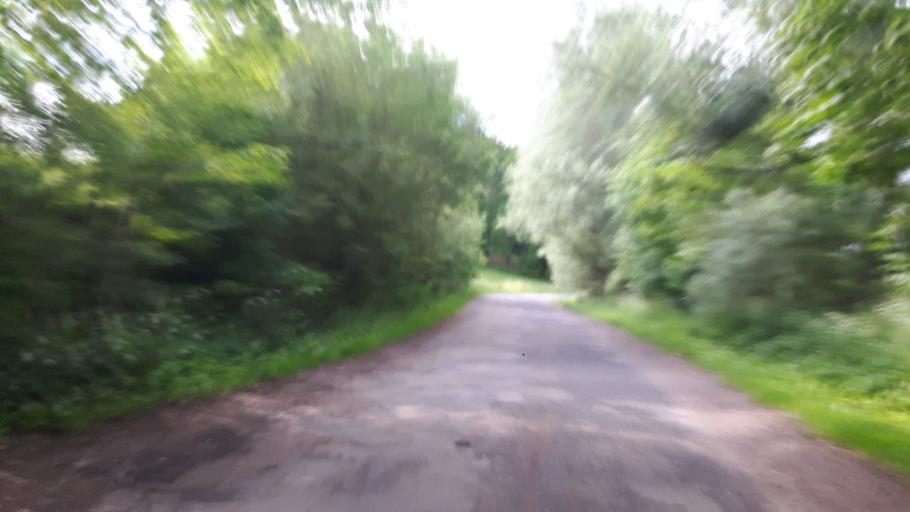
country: PL
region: West Pomeranian Voivodeship
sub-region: Powiat gryficki
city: Gryfice
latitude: 53.8319
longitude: 15.1464
